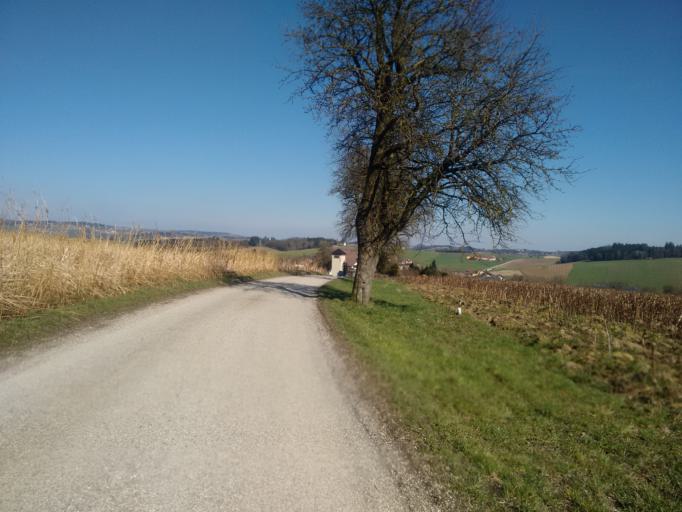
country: AT
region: Upper Austria
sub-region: Politischer Bezirk Grieskirchen
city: Bad Schallerbach
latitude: 48.2029
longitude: 13.9467
